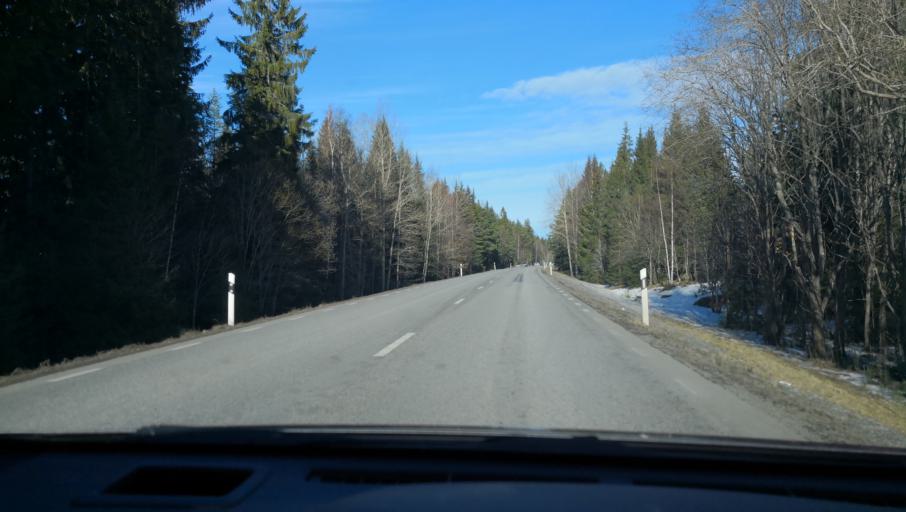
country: SE
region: Uppsala
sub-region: Uppsala Kommun
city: Vattholma
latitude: 60.0182
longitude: 17.7448
